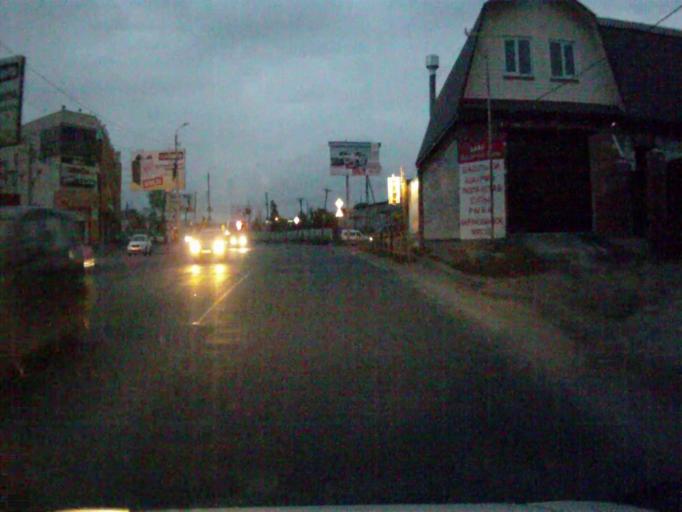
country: RU
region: Chelyabinsk
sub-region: Gorod Chelyabinsk
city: Chelyabinsk
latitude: 55.1544
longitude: 61.3024
